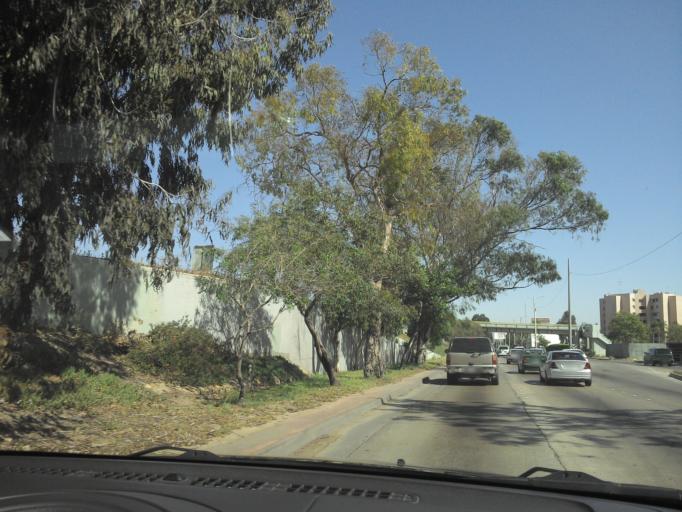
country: MX
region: Baja California
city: Tijuana
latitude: 32.5213
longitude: -117.0069
